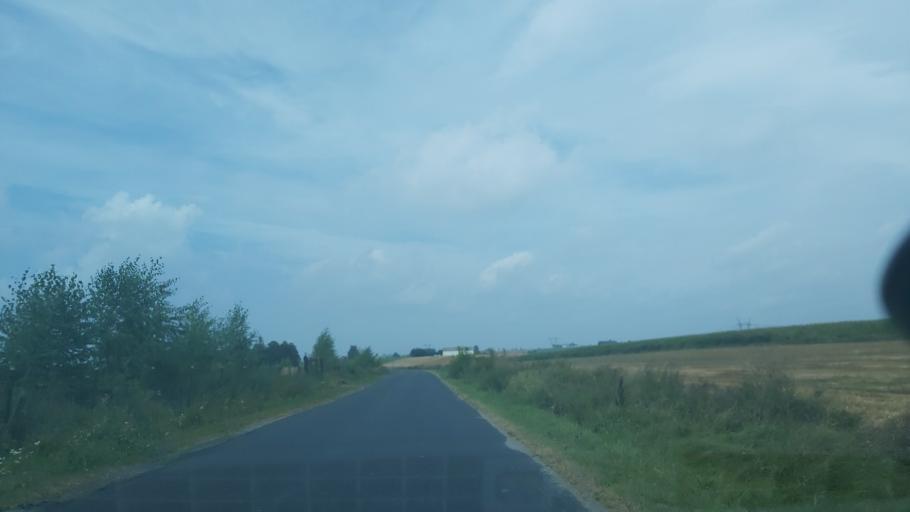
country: PL
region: Kujawsko-Pomorskie
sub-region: Powiat golubsko-dobrzynski
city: Zbojno
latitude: 53.0346
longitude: 19.1765
